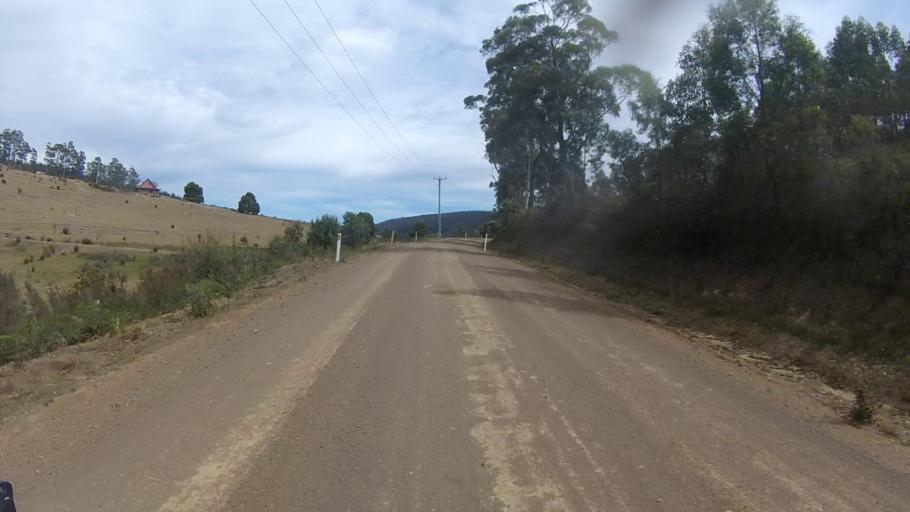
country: AU
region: Tasmania
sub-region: Sorell
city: Sorell
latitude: -42.7579
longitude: 147.8007
